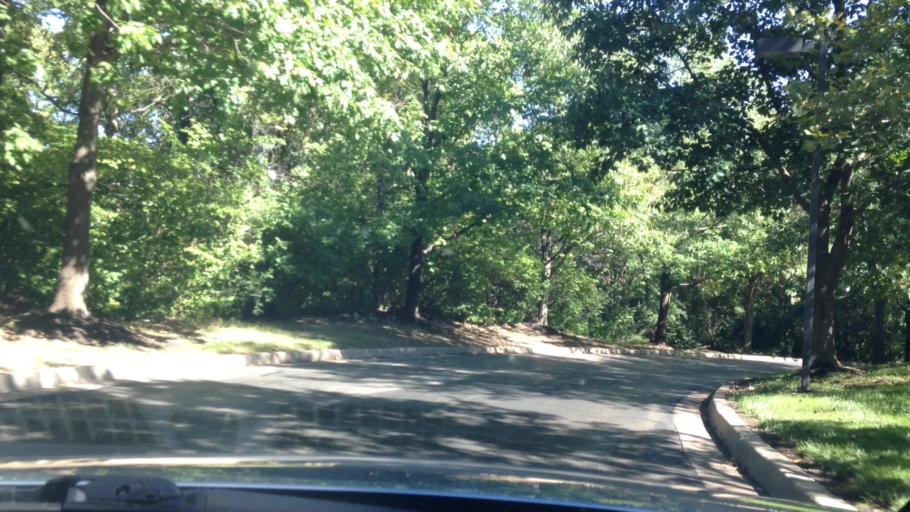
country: US
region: Kansas
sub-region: Johnson County
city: Roeland Park
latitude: 39.0465
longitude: -94.6419
